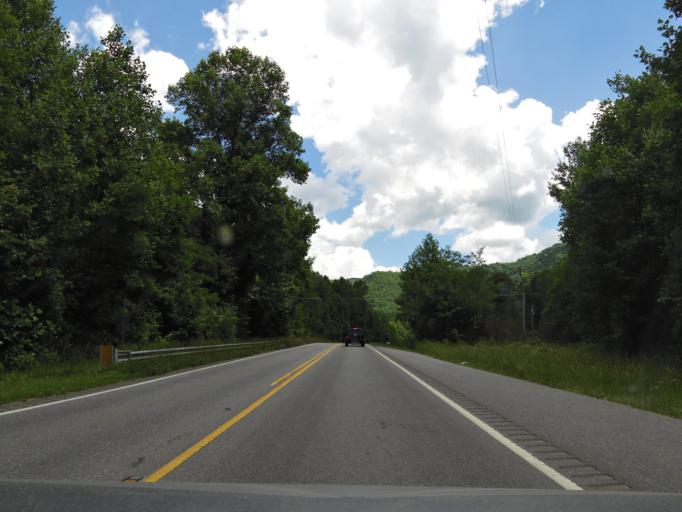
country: US
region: North Carolina
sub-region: Graham County
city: Robbinsville
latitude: 35.2747
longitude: -83.7572
